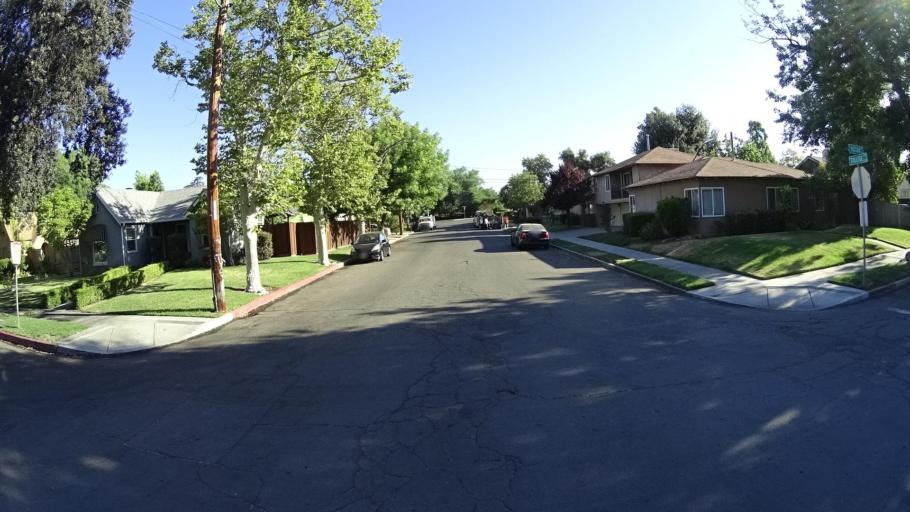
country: US
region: California
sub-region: Fresno County
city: Fresno
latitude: 36.7713
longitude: -119.7974
